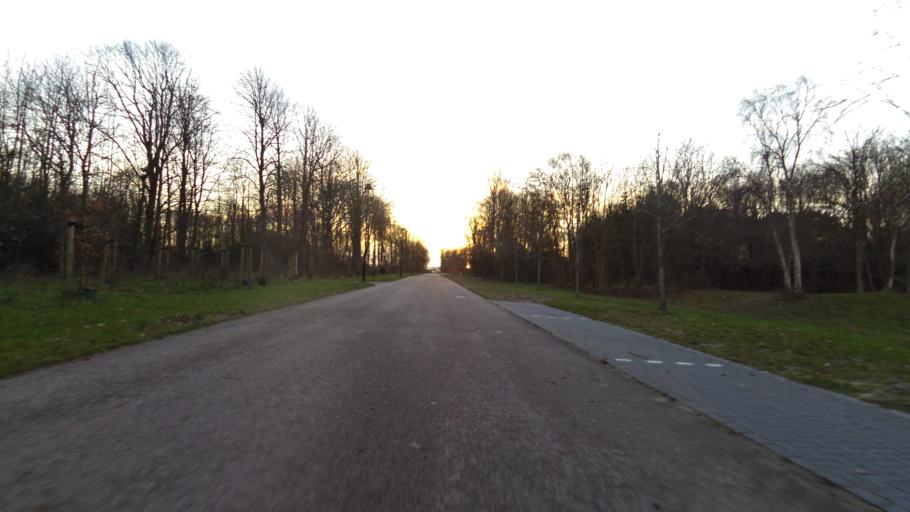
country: NL
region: South Holland
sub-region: Gemeente Noordwijkerhout
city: Noordwijkerhout
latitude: 52.2772
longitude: 4.4892
